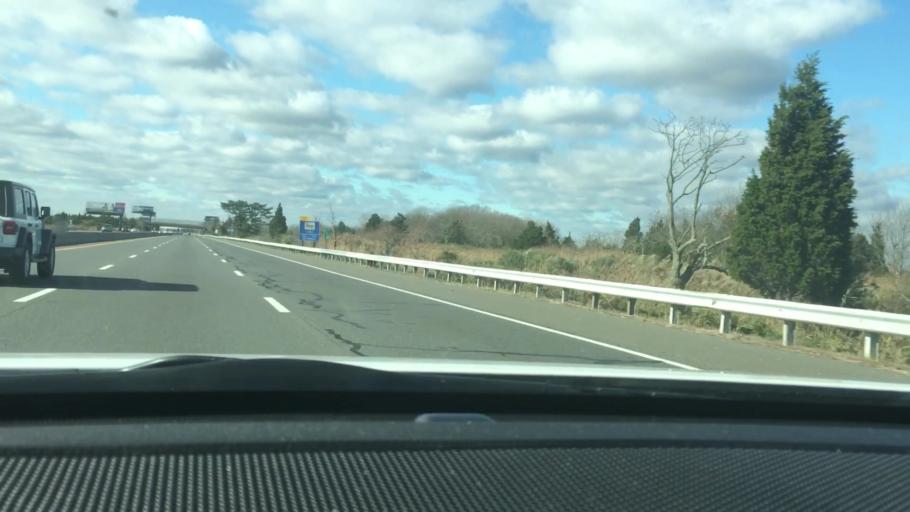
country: US
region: New Jersey
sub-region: Atlantic County
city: Ventnor City
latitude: 39.3728
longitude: -74.4720
